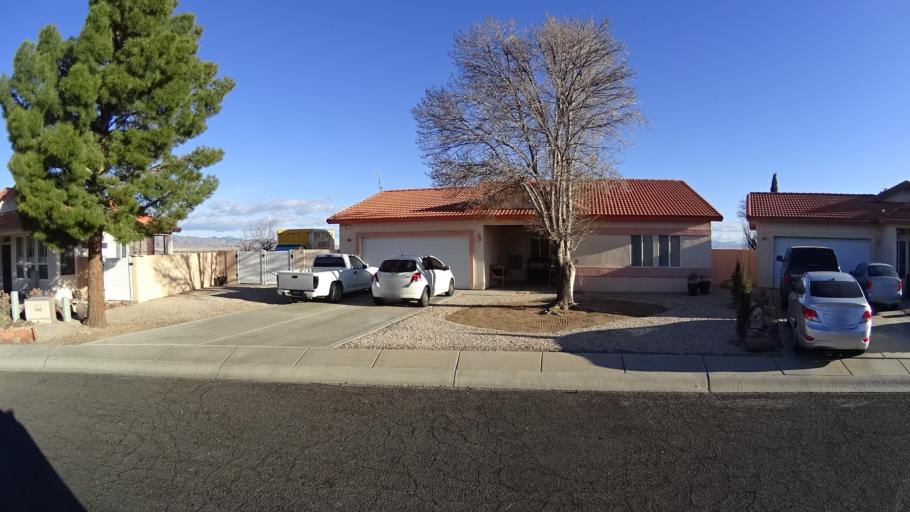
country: US
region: Arizona
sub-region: Mohave County
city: New Kingman-Butler
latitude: 35.2254
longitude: -113.9899
